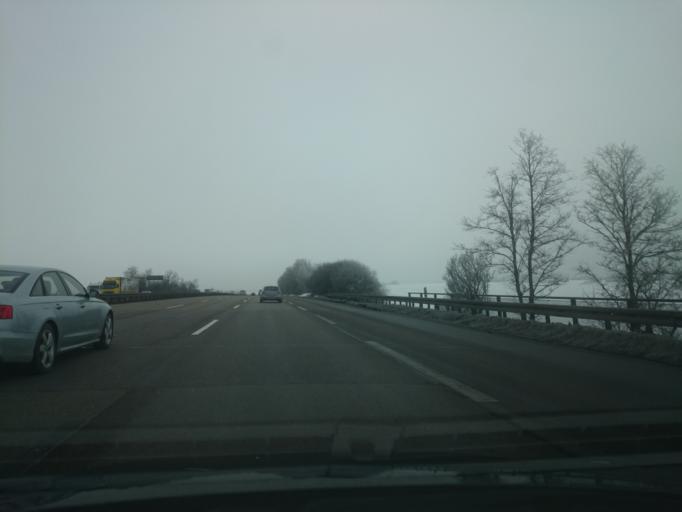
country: DE
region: Bavaria
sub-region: Upper Bavaria
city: Stammham
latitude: 48.8356
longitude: 11.4705
